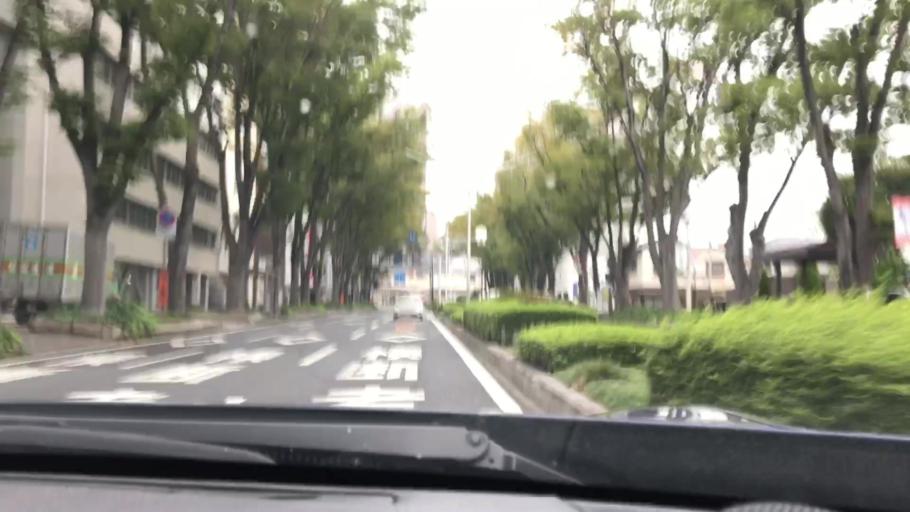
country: JP
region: Gunma
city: Maebashi-shi
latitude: 36.3868
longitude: 139.0726
